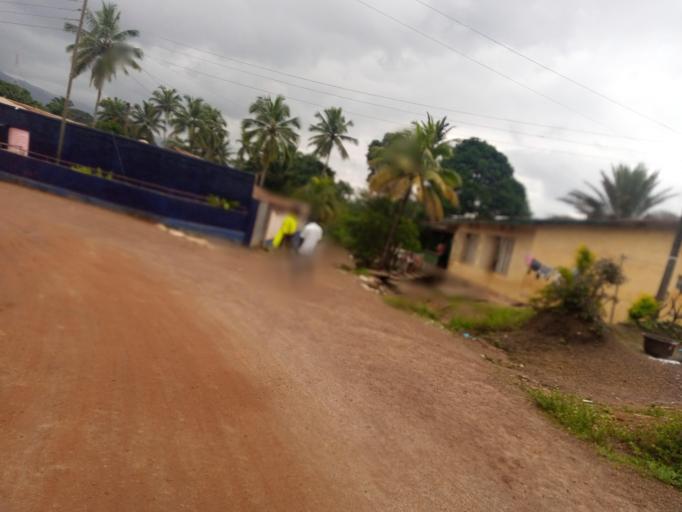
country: SL
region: Eastern Province
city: Kenema
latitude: 7.8622
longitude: -11.1919
